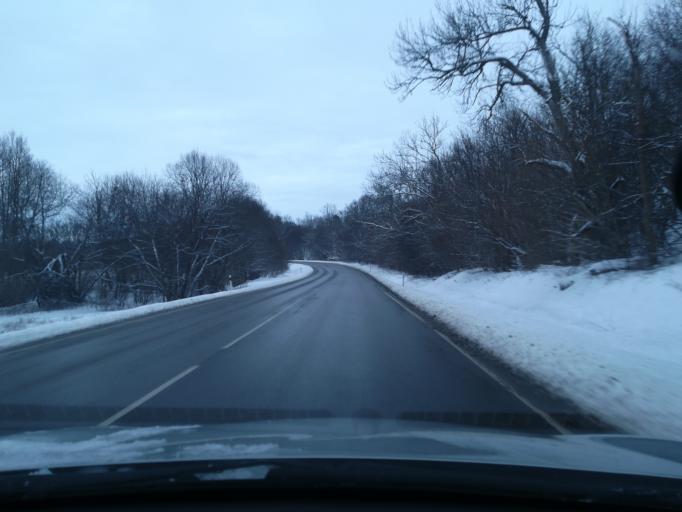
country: EE
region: Harju
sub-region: Keila linn
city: Keila
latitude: 59.4188
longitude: 24.3360
